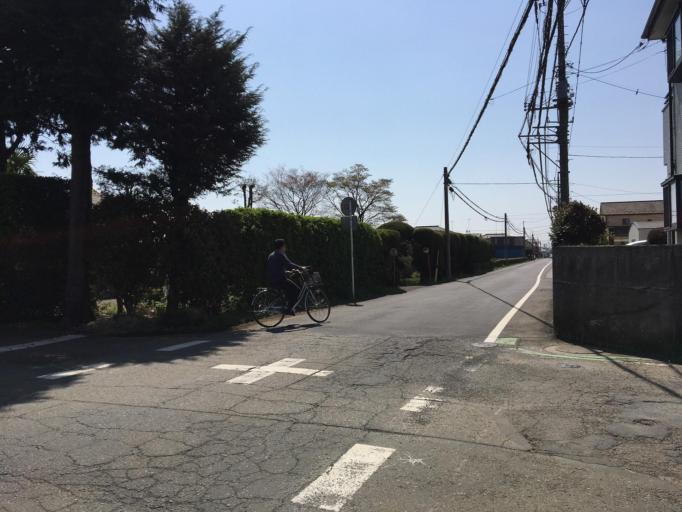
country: JP
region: Saitama
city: Sakado
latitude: 35.9090
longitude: 139.3654
